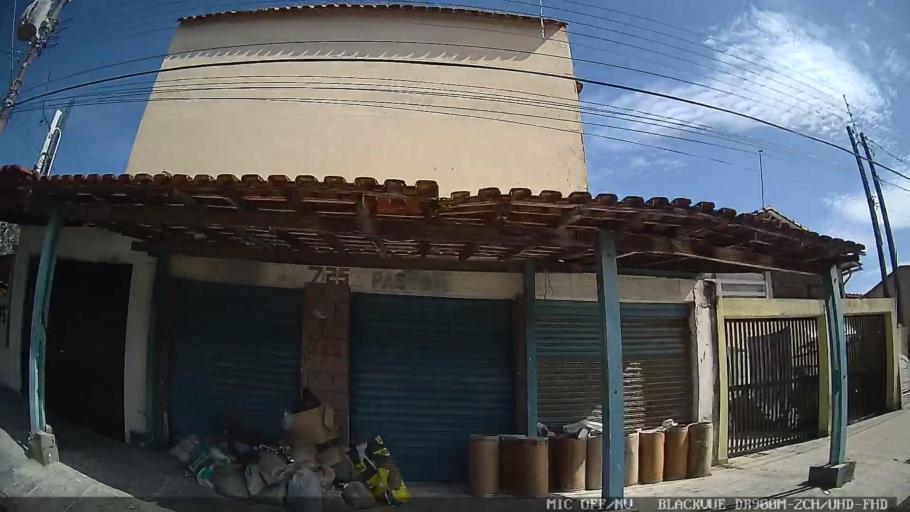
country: BR
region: Sao Paulo
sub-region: Itanhaem
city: Itanhaem
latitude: -24.1520
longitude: -46.7381
